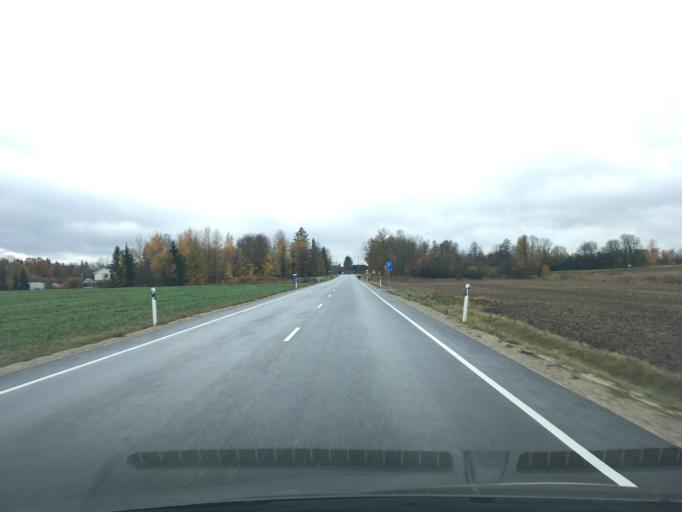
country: EE
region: Jogevamaa
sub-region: Tabivere vald
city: Tabivere
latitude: 58.4330
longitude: 26.4887
